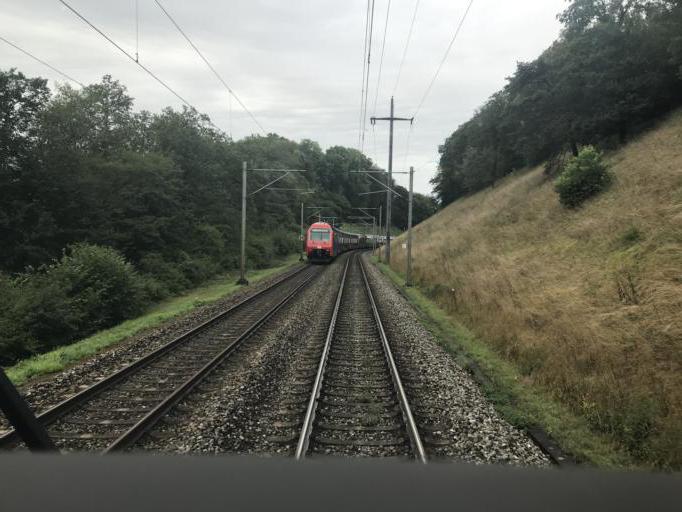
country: CH
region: Zurich
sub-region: Bezirk Buelach
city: Hochfelden
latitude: 47.5422
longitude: 8.5235
